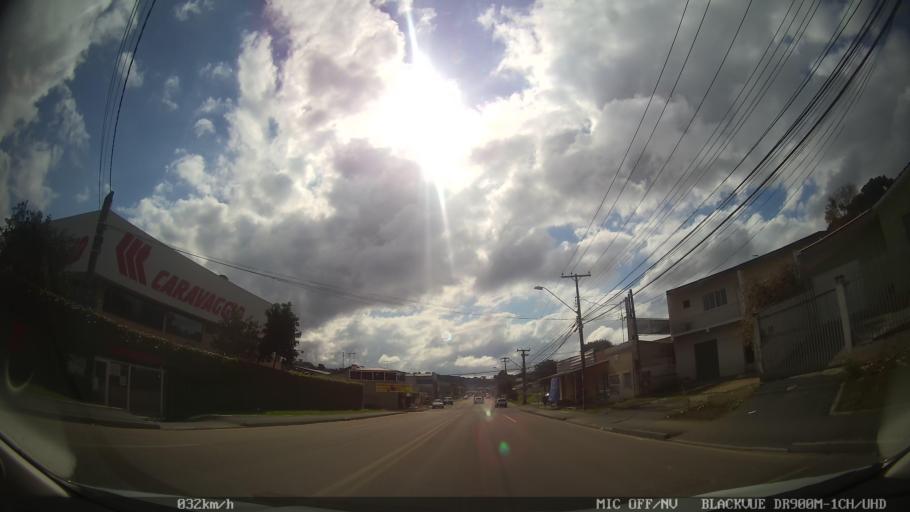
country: BR
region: Parana
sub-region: Pinhais
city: Pinhais
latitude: -25.3659
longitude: -49.1954
